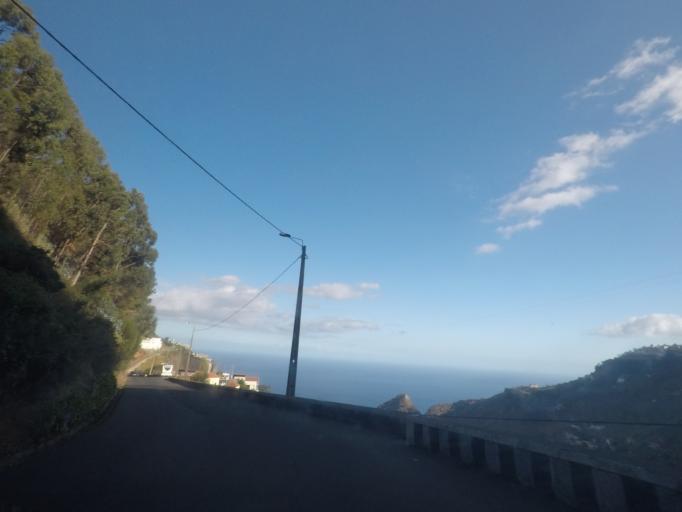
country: PT
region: Madeira
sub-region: Ribeira Brava
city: Campanario
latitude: 32.6673
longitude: -16.9997
